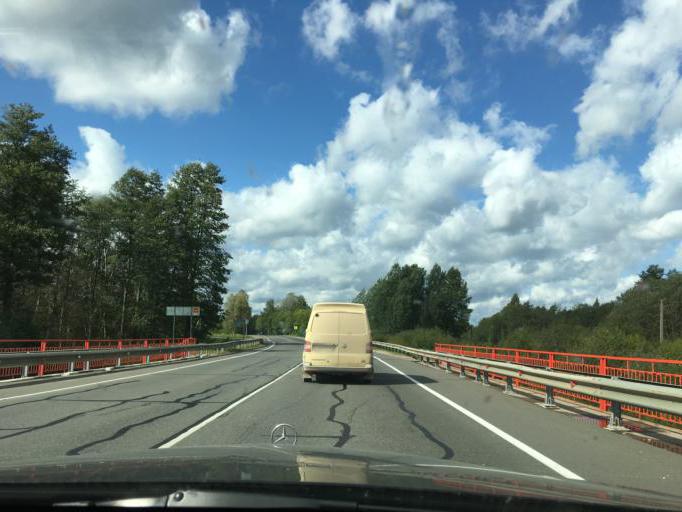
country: RU
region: Pskov
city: Pustoshka
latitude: 56.4003
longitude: 29.2332
